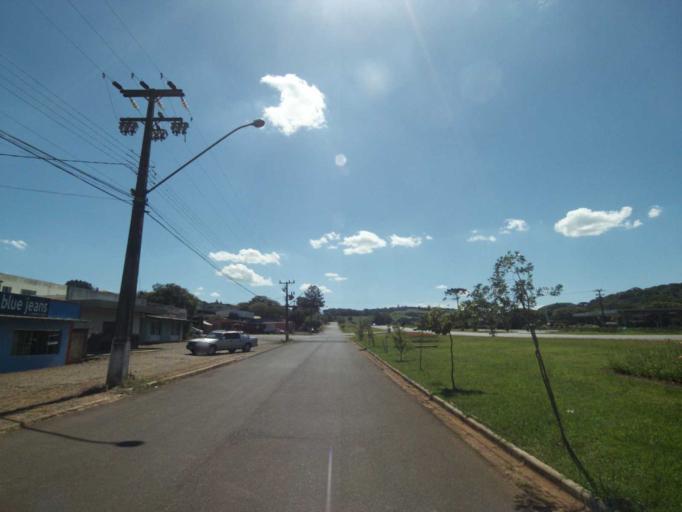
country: BR
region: Parana
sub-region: Laranjeiras Do Sul
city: Laranjeiras do Sul
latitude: -25.3785
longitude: -52.2018
